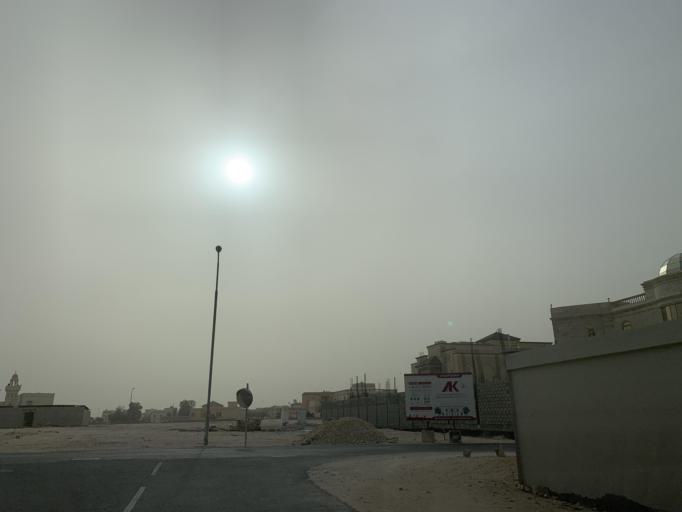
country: BH
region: Central Governorate
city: Madinat Hamad
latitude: 26.1395
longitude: 50.5248
